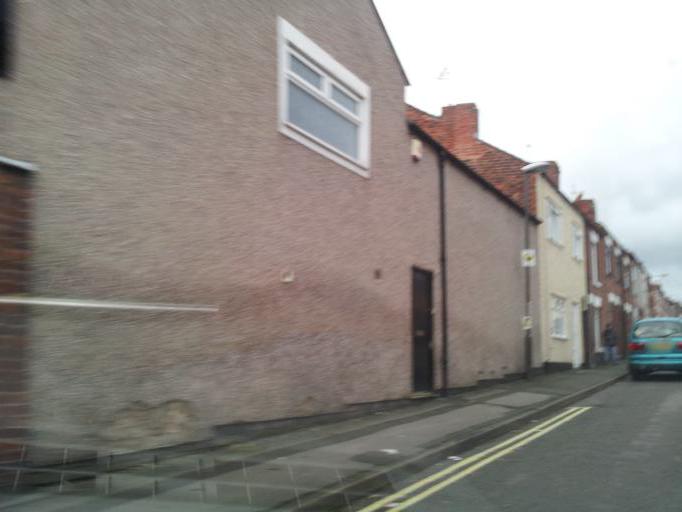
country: GB
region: England
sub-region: Nottinghamshire
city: Eastwood
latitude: 52.9868
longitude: -1.3083
